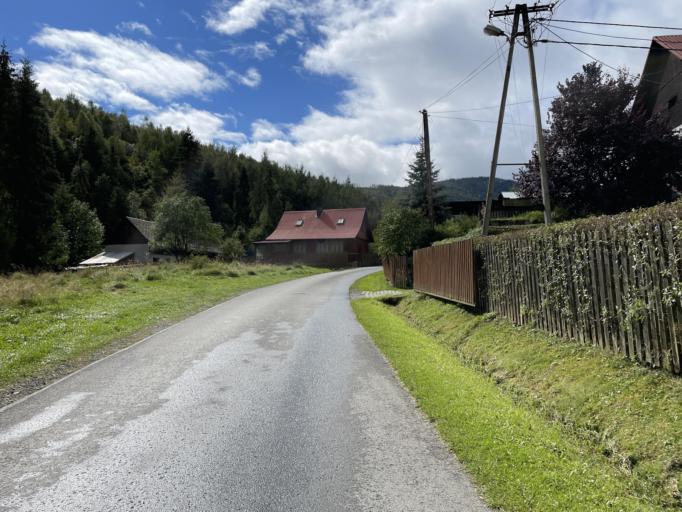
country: PL
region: Silesian Voivodeship
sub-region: Powiat zywiecki
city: Ujsoly
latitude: 49.4783
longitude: 19.1309
